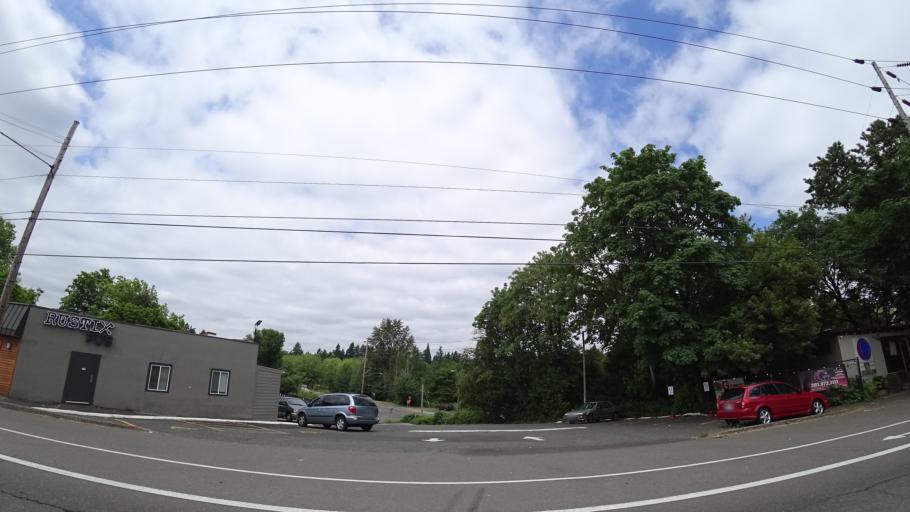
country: US
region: Oregon
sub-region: Clackamas County
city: Lake Oswego
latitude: 45.4646
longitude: -122.6996
